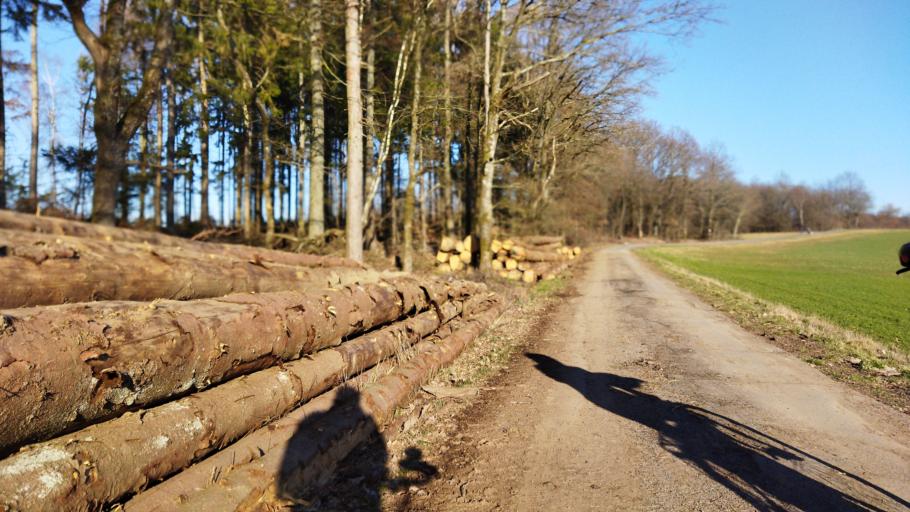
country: DE
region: Rheinland-Pfalz
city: Selchenbach
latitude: 49.4982
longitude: 7.2839
